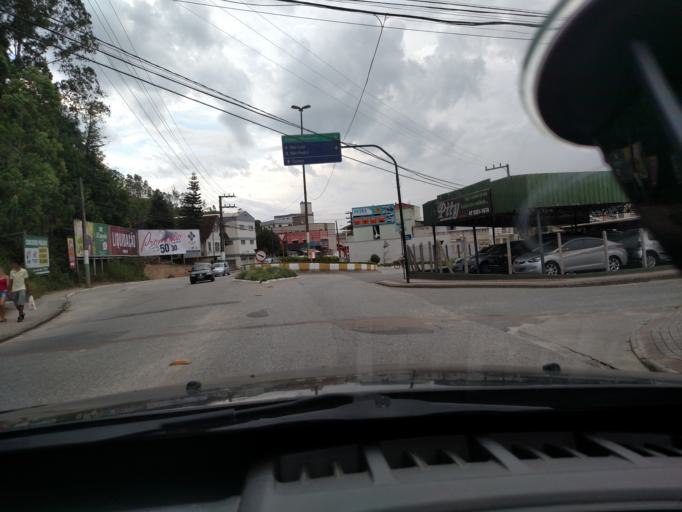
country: BR
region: Santa Catarina
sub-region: Brusque
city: Brusque
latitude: -27.0823
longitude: -48.9000
